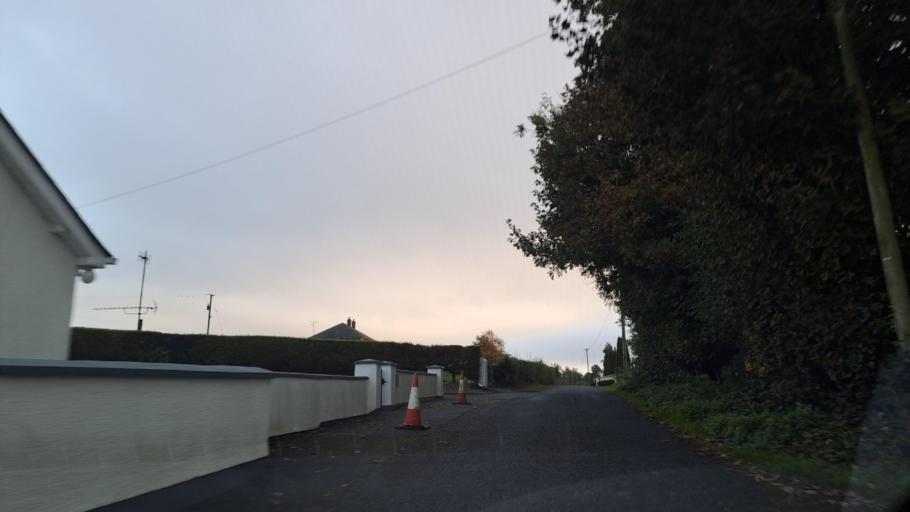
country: IE
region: Ulster
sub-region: County Monaghan
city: Carrickmacross
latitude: 53.9810
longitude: -6.6780
